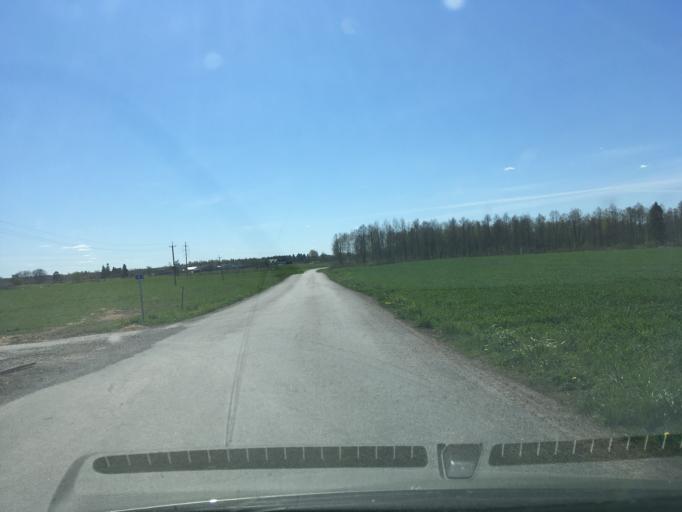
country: EE
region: Harju
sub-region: Raasiku vald
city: Arukula
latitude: 59.3884
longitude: 25.0800
